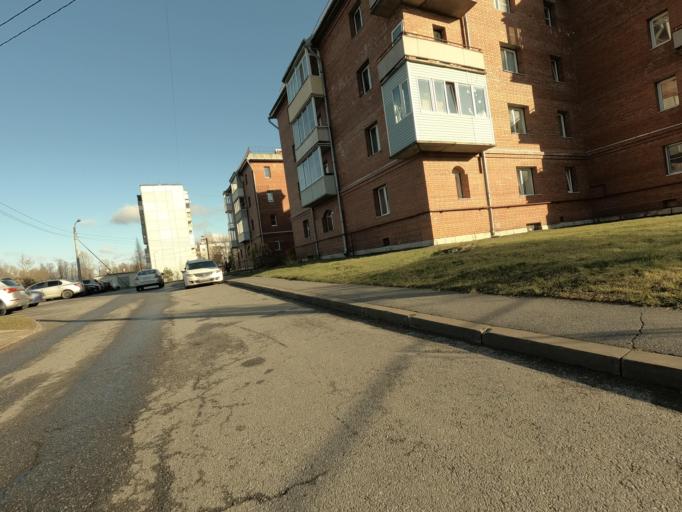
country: RU
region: St.-Petersburg
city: Krasnogvargeisky
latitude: 59.9851
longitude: 30.5197
